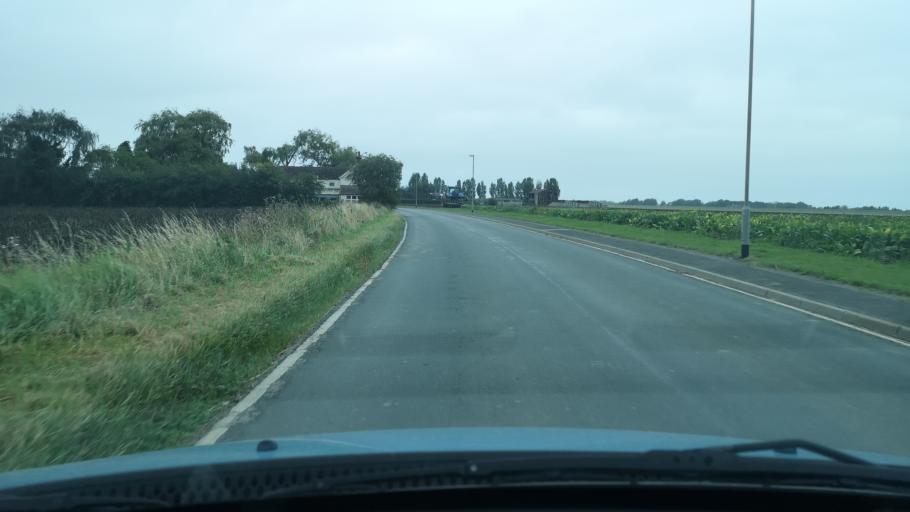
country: GB
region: England
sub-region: East Riding of Yorkshire
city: Laxton
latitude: 53.7000
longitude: -0.8042
